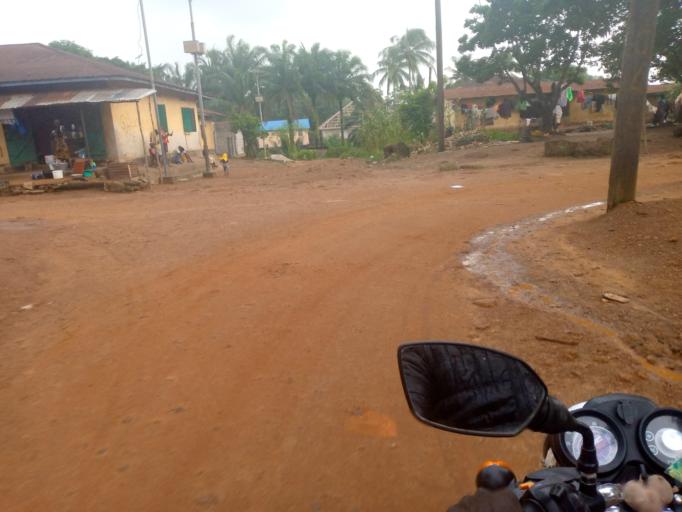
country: SL
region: Eastern Province
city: Kenema
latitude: 7.8851
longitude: -11.1818
